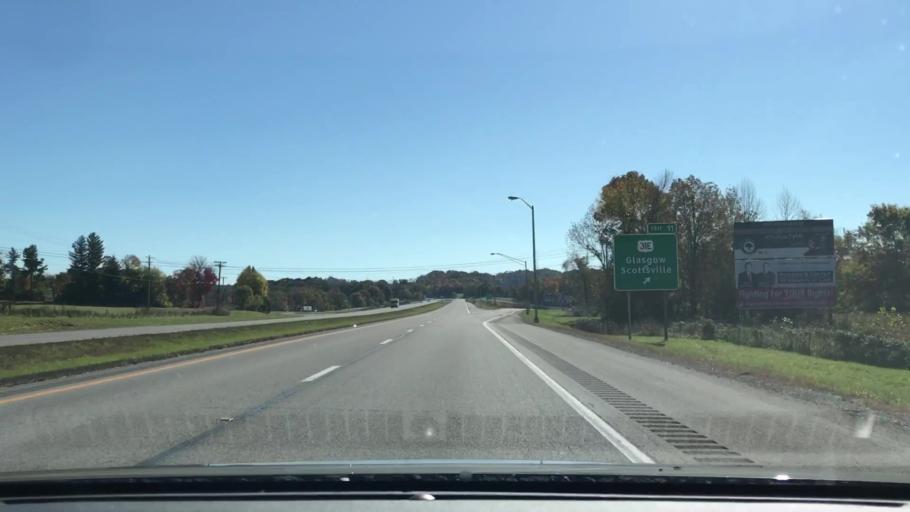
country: US
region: Kentucky
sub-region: Barren County
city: Glasgow
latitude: 36.9809
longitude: -85.9403
